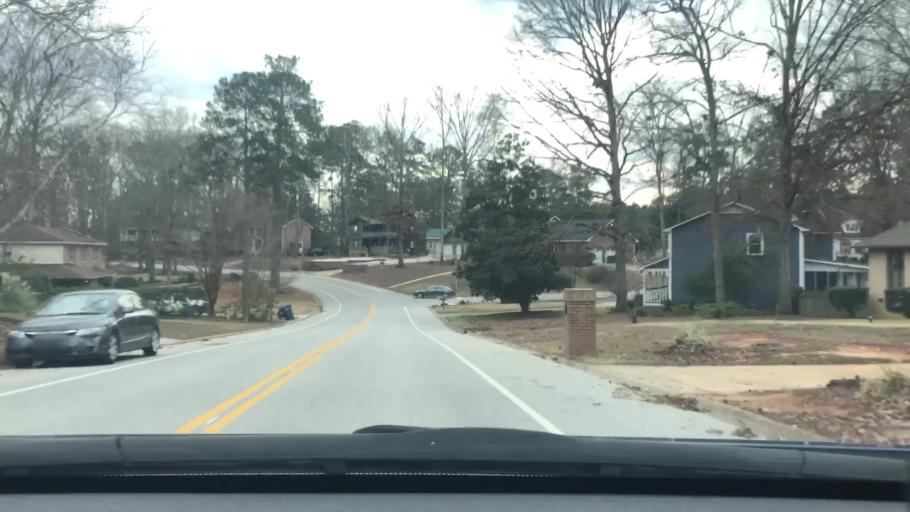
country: US
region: South Carolina
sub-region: Lexington County
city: Irmo
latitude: 34.0778
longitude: -81.1653
